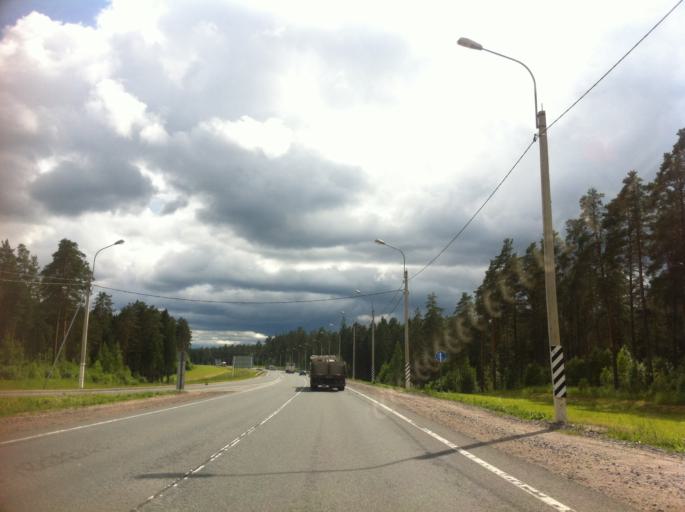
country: RU
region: Leningrad
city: Luga
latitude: 58.7262
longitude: 29.8793
